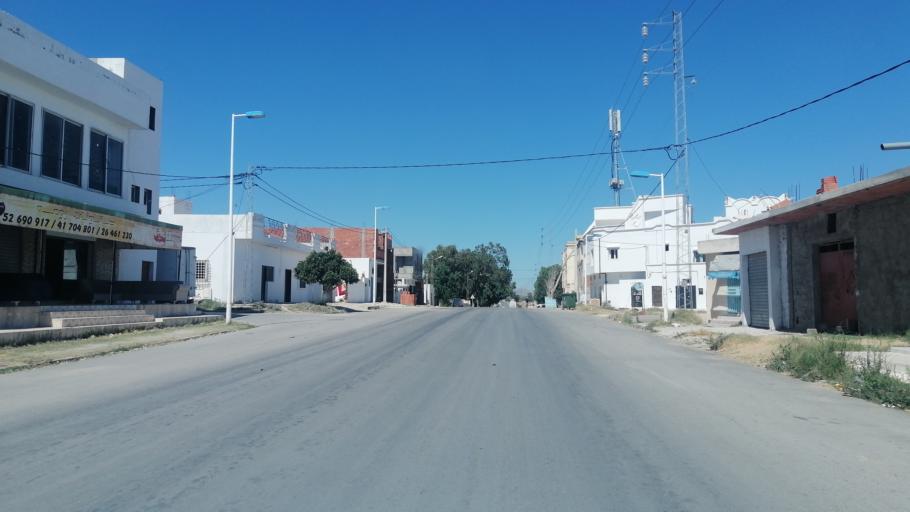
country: TN
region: Al Qayrawan
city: Sbikha
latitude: 36.1246
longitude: 10.0945
